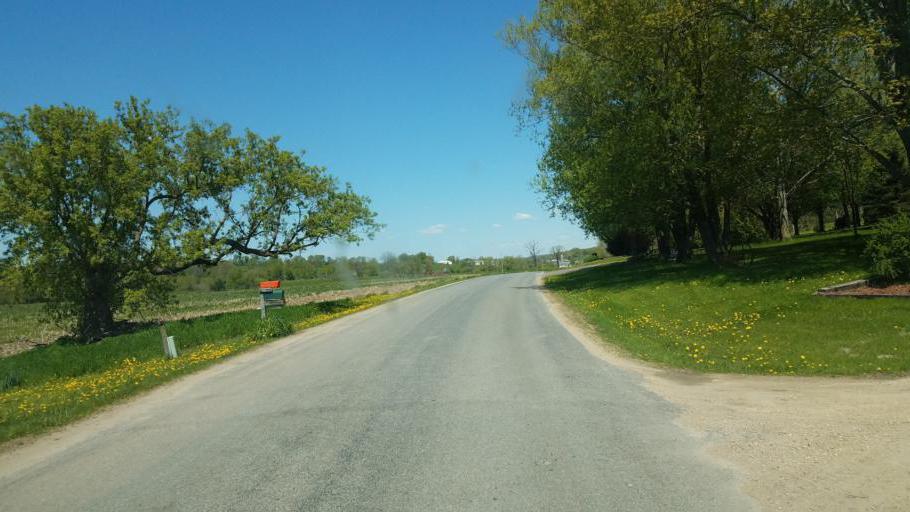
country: US
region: Wisconsin
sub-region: Vernon County
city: Hillsboro
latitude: 43.6213
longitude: -90.3704
